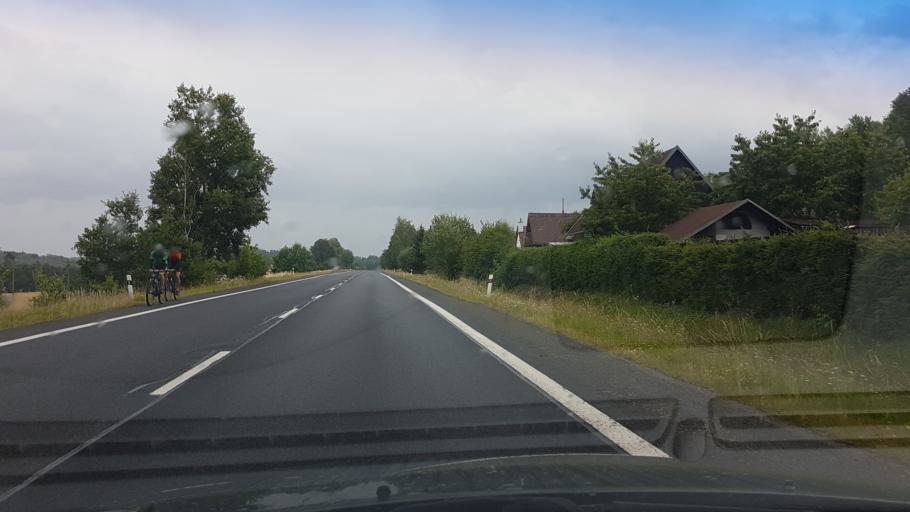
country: CZ
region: Karlovarsky
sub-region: Okres Cheb
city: Frantiskovy Lazne
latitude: 50.0814
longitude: 12.3211
